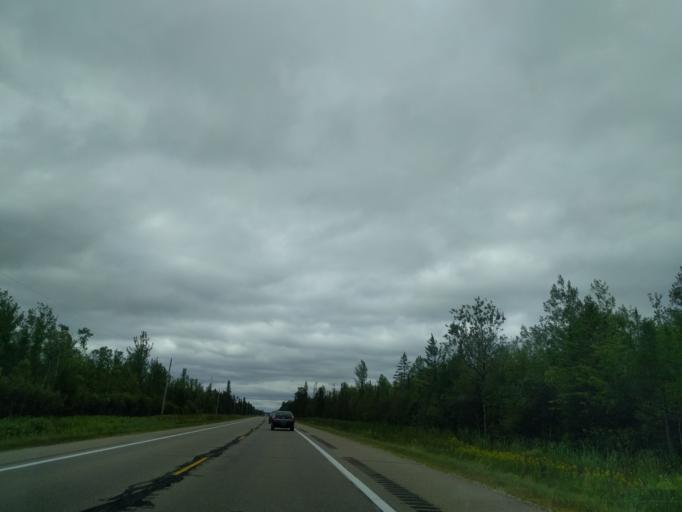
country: US
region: Michigan
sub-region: Delta County
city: Escanaba
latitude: 45.6319
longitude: -87.2040
